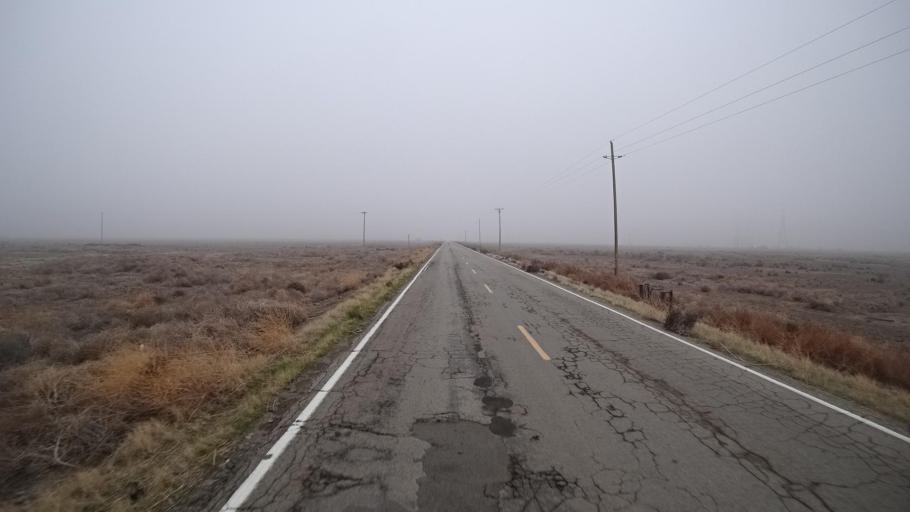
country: US
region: California
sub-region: Kern County
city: Lost Hills
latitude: 35.6109
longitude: -119.6174
